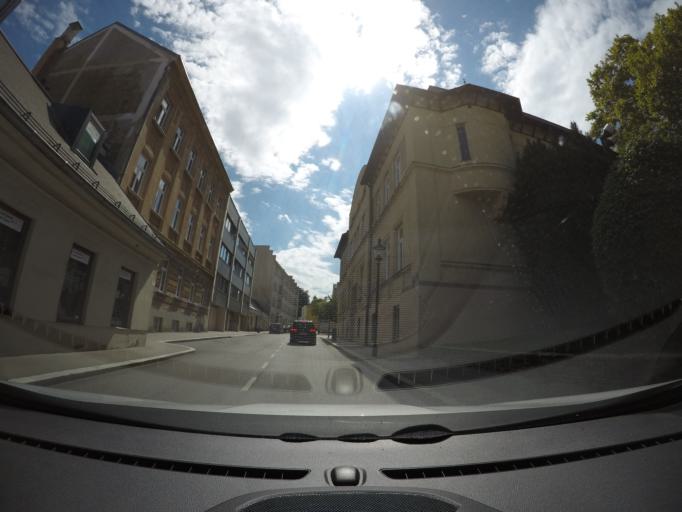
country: AT
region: Lower Austria
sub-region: Politischer Bezirk Modling
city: Perchtoldsdorf
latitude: 48.1882
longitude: 16.2664
